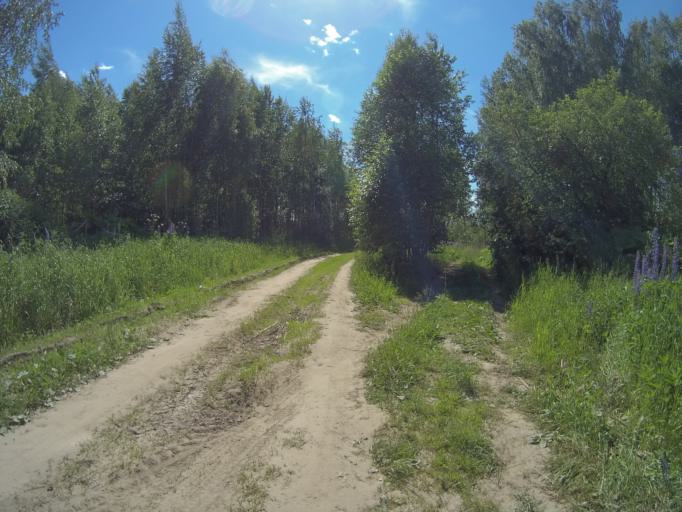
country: RU
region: Vladimir
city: Golovino
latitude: 55.9787
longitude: 40.3892
